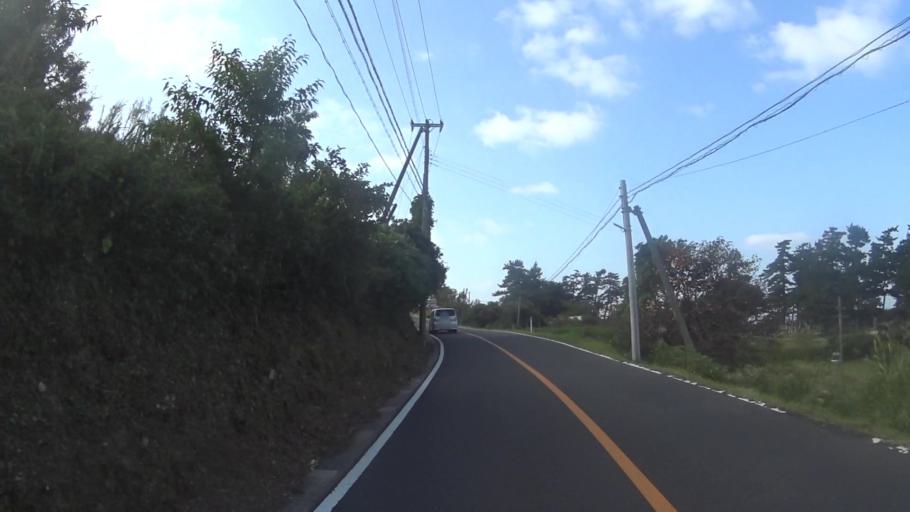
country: JP
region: Kyoto
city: Miyazu
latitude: 35.7506
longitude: 135.1594
